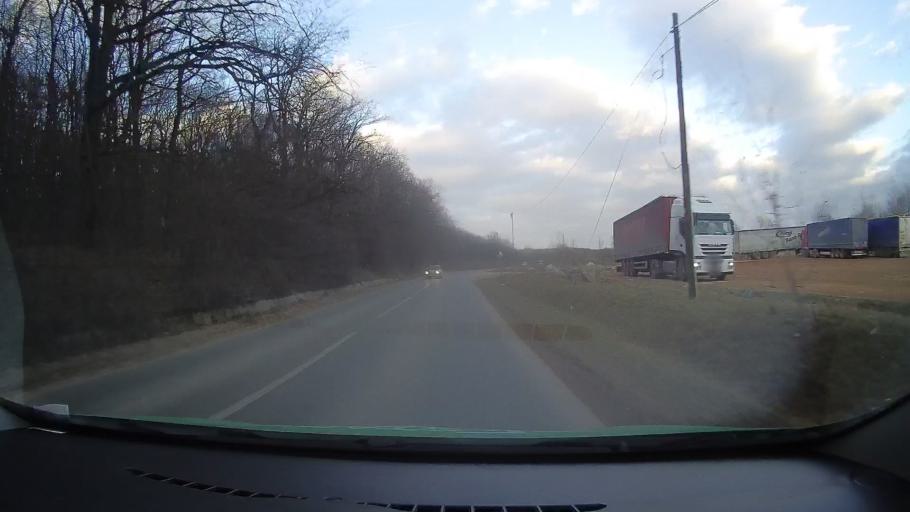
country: RO
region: Dambovita
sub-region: Comuna Gura Ocnitei
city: Gura Ocnitei
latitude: 44.9460
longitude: 25.5865
